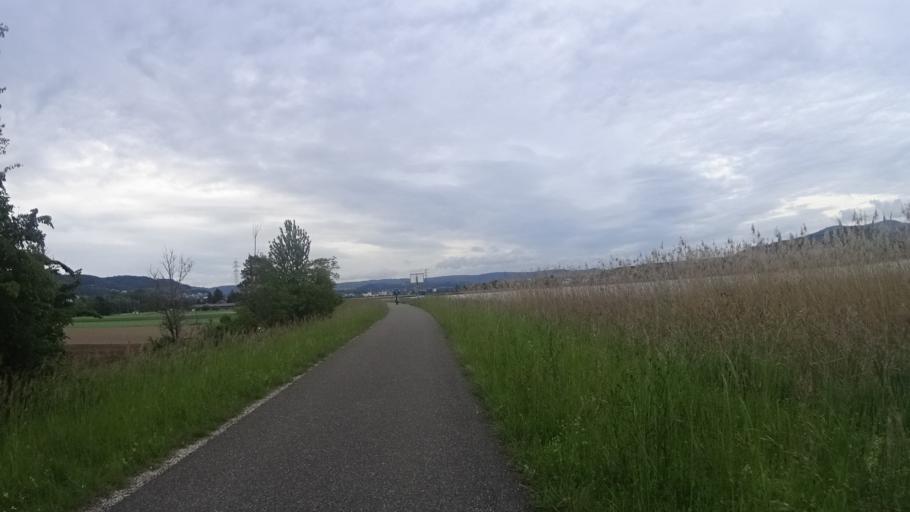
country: CH
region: Aargau
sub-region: Bezirk Zurzach
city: Koblenz
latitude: 47.5899
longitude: 8.2318
